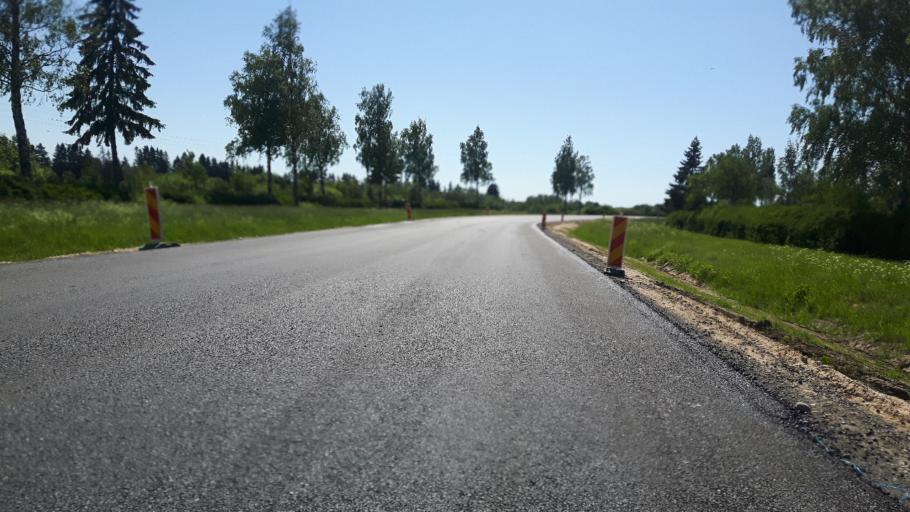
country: EE
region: Paernumaa
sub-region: Sindi linn
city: Sindi
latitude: 58.4253
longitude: 24.7247
